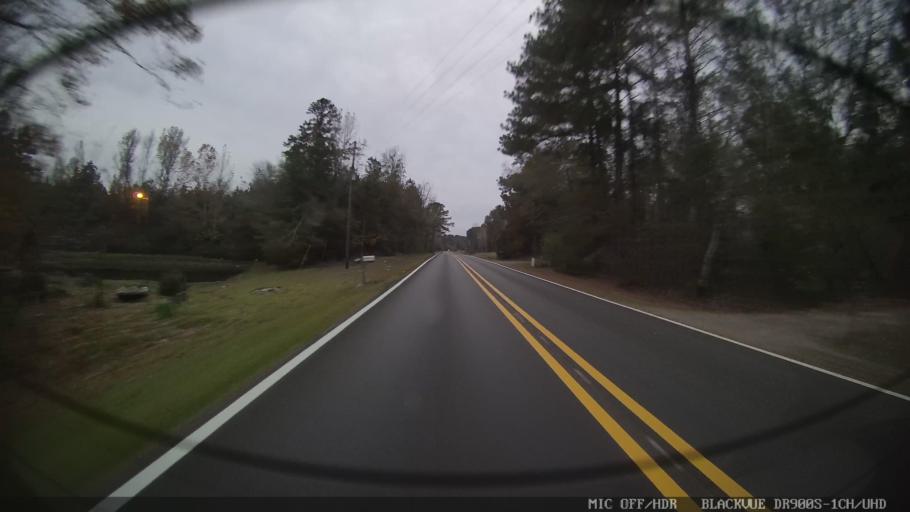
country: US
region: Mississippi
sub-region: Clarke County
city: Quitman
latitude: 32.0494
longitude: -88.6930
